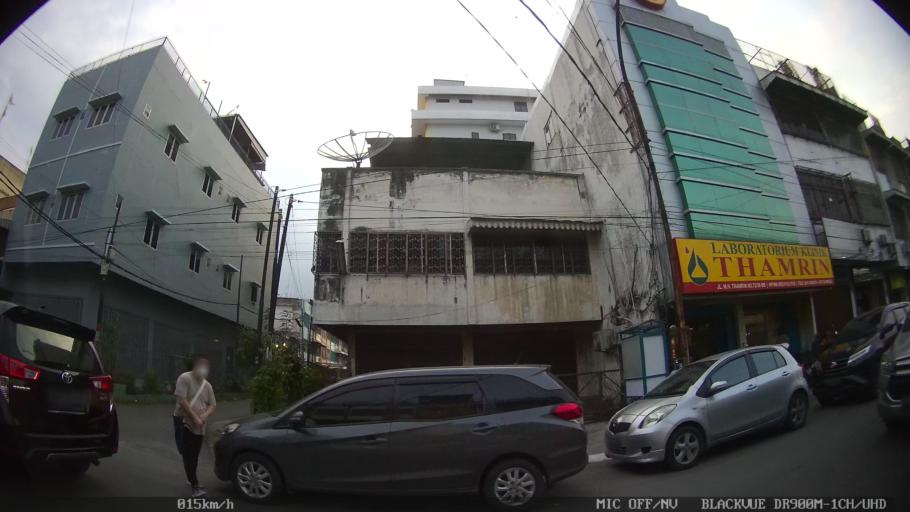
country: ID
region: North Sumatra
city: Medan
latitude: 3.5931
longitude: 98.6878
